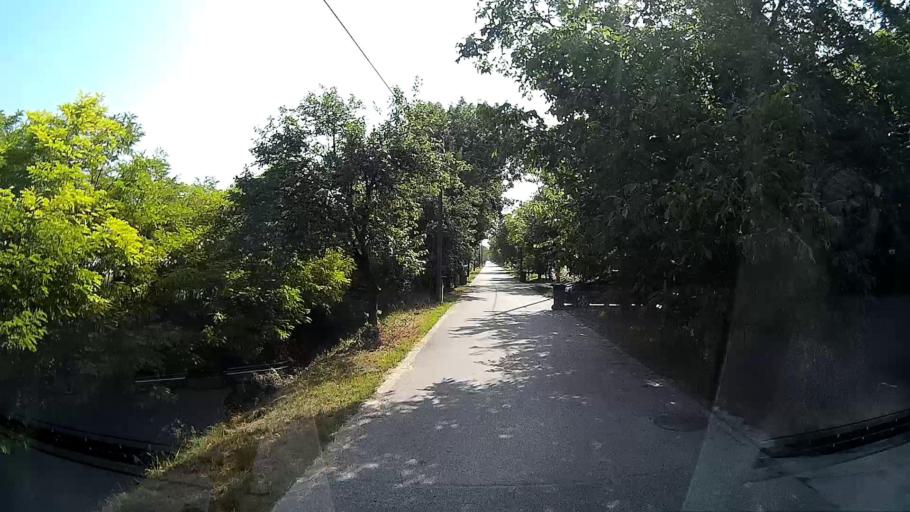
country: HU
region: Pest
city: Budakalasz
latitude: 47.6326
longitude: 19.0510
